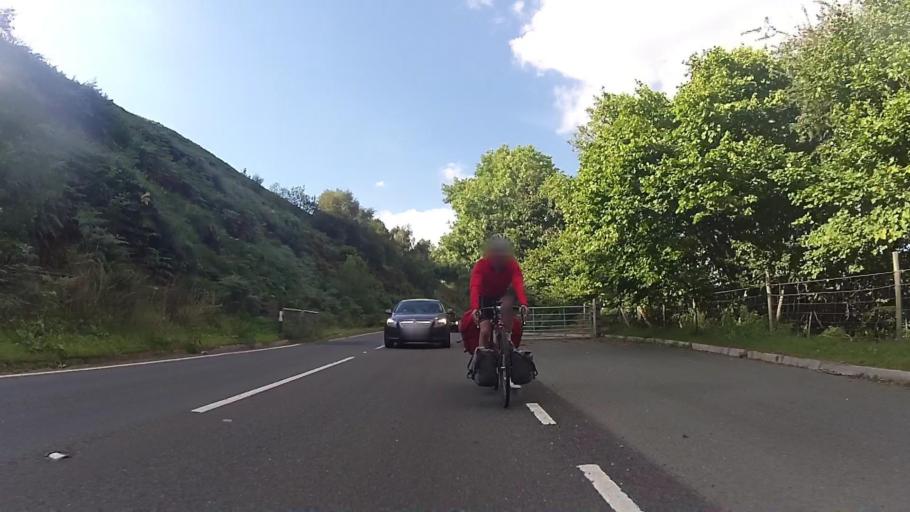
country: GB
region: Wales
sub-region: Denbighshire
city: Llangollen
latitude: 53.0082
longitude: -3.1958
